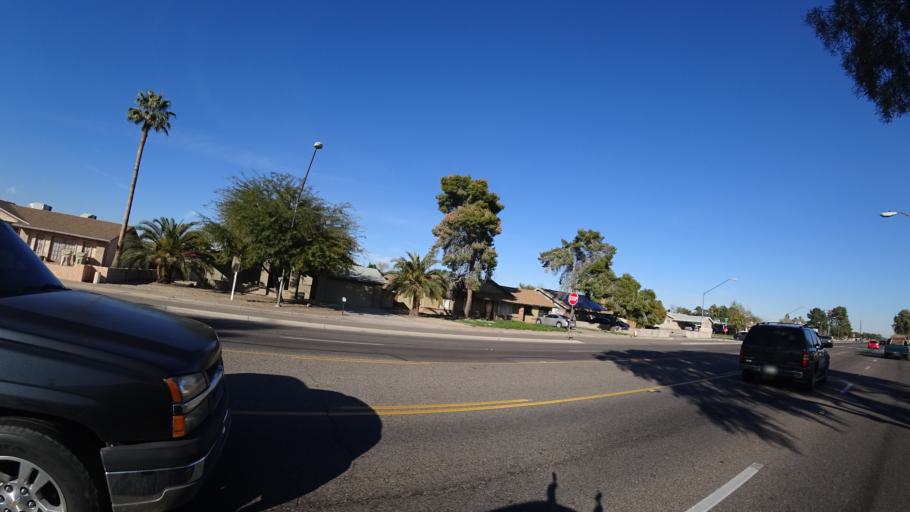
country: US
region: Arizona
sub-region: Maricopa County
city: Glendale
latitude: 33.5234
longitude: -112.2170
